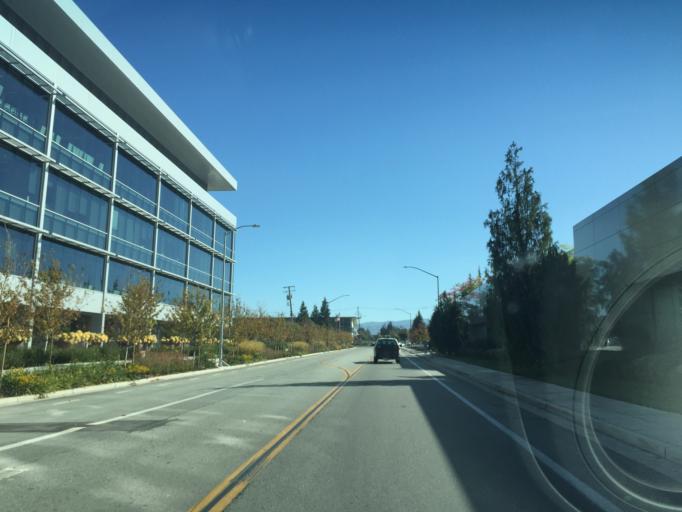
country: US
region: California
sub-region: Santa Clara County
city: Mountain View
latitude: 37.4152
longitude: -122.0757
